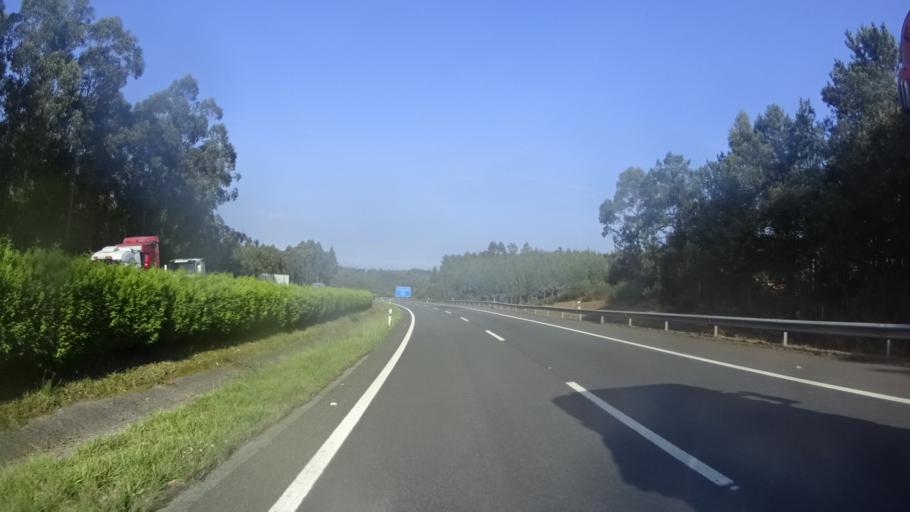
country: ES
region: Galicia
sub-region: Provincia da Coruna
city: Aranga
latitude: 43.2236
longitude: -8.0563
